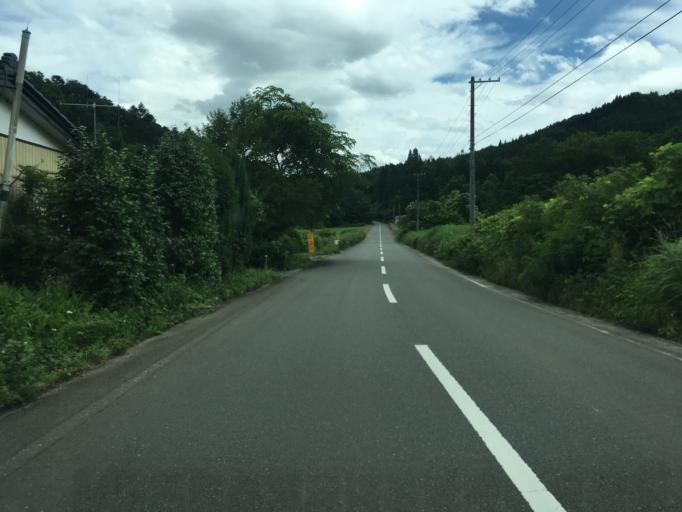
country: JP
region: Fukushima
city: Namie
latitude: 37.6872
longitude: 140.8906
